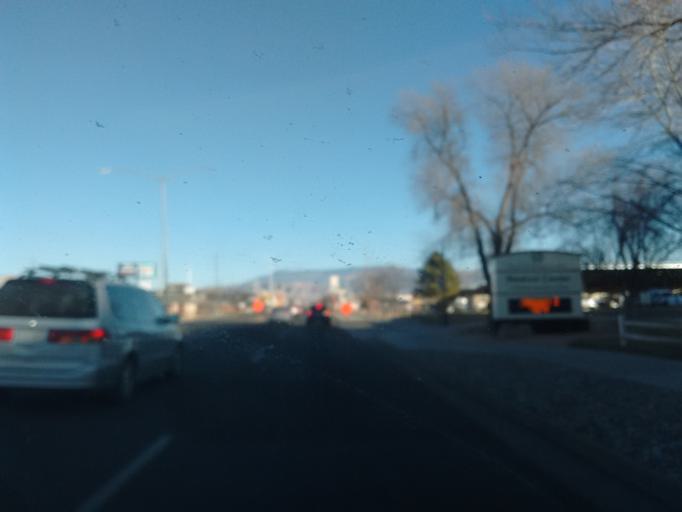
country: US
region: Colorado
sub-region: Mesa County
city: Grand Junction
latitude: 39.0773
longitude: -108.5401
